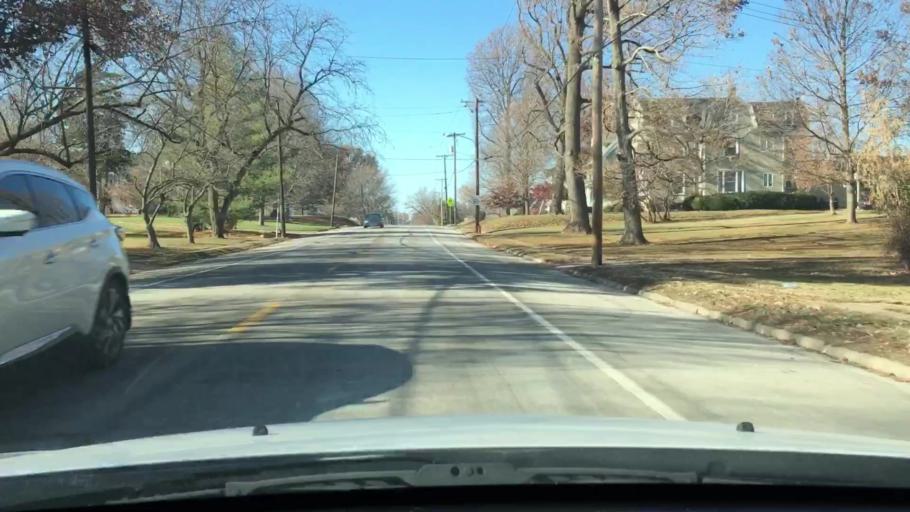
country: US
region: Illinois
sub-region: Pike County
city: Pittsfield
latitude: 39.6068
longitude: -90.7985
